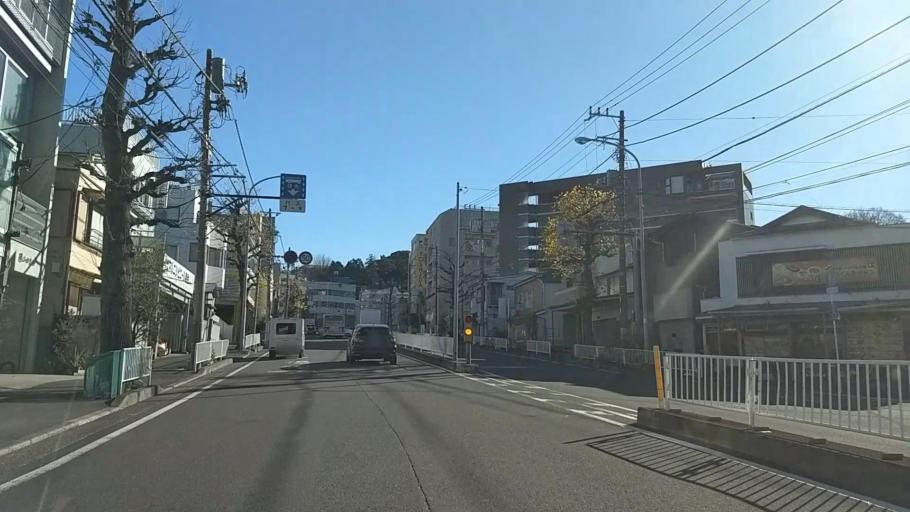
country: JP
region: Kanagawa
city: Yokohama
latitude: 35.4511
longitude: 139.6230
